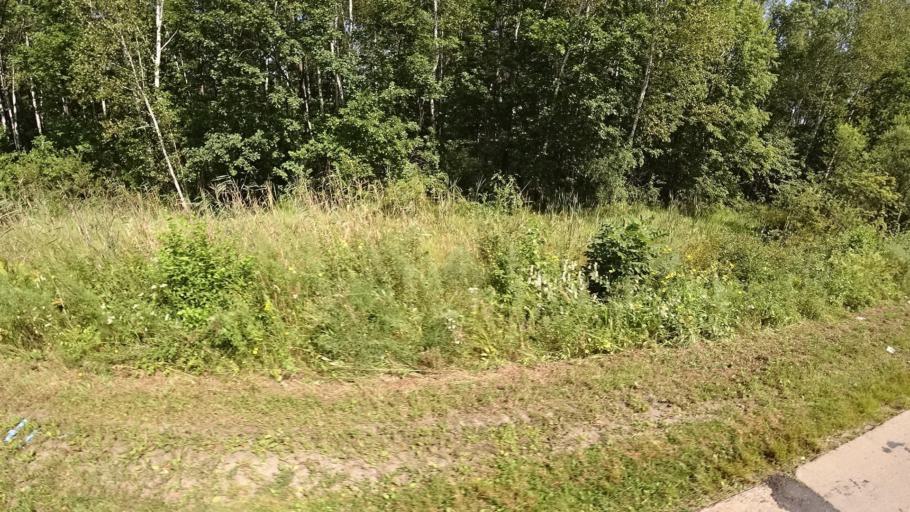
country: RU
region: Khabarovsk Krai
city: Khor
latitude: 47.9800
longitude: 135.0991
